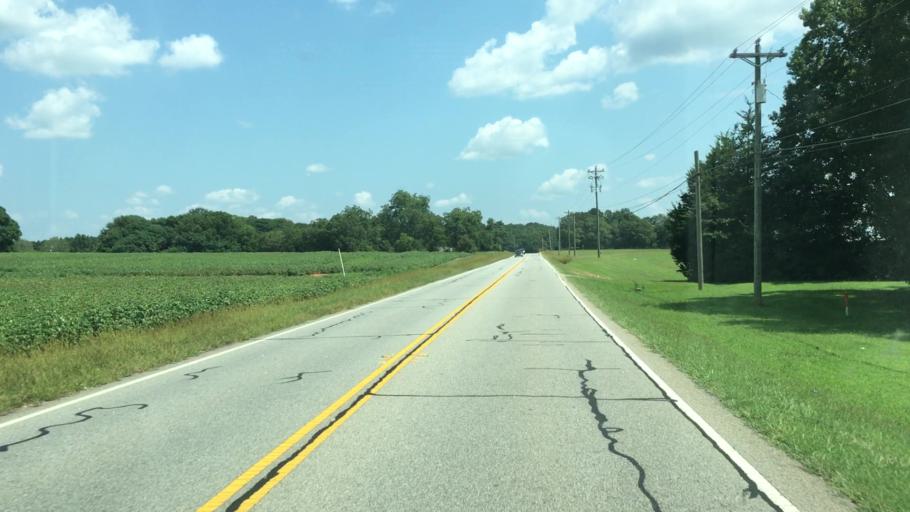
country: US
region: Georgia
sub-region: Oconee County
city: Bogart
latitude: 33.8723
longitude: -83.5107
